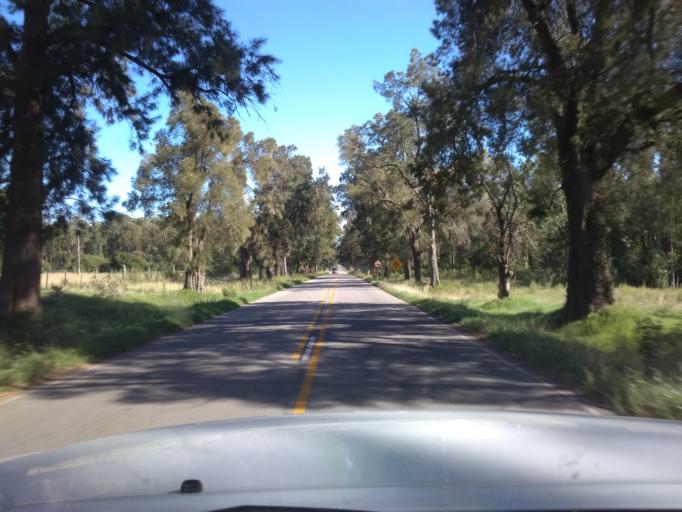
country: UY
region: Canelones
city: San Bautista
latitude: -34.3821
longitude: -55.9595
